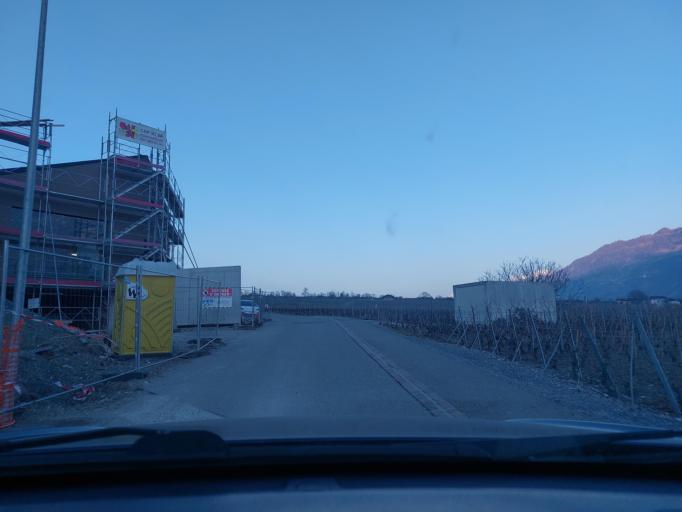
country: CH
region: Valais
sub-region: Martigny District
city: Leytron
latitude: 46.1877
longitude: 7.2146
